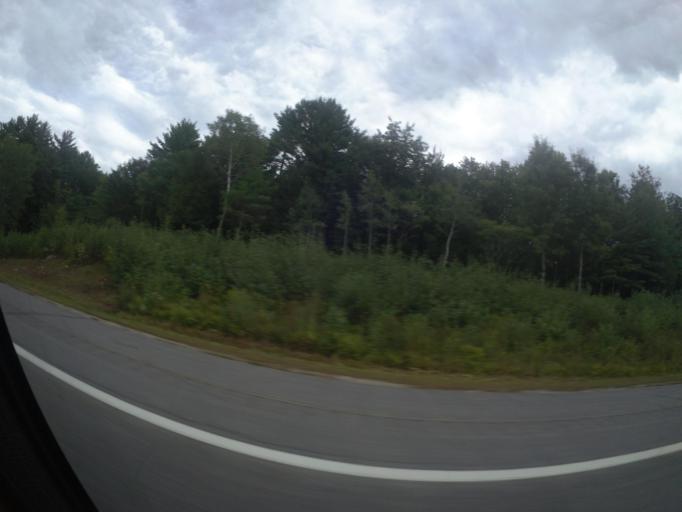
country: US
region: New Hampshire
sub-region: Merrimack County
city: Chichester
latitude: 43.2354
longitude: -71.4620
